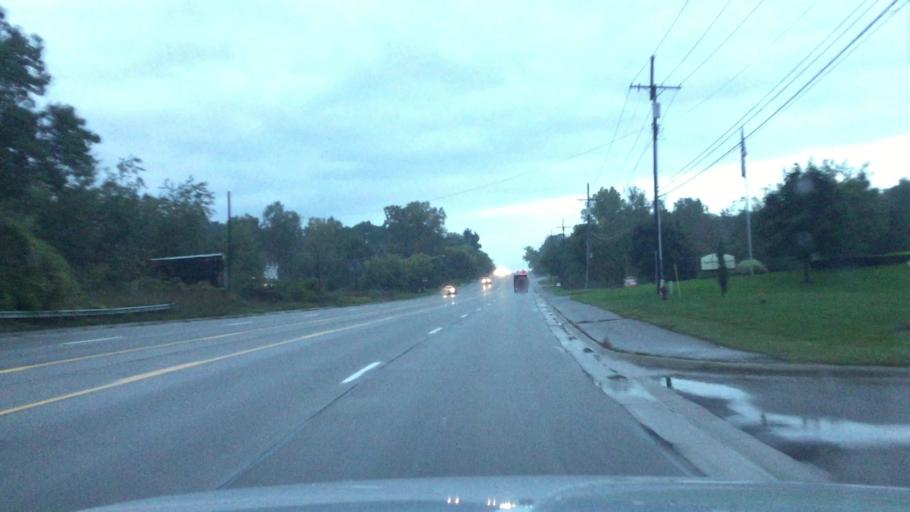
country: US
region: Michigan
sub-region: Oakland County
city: Clarkston
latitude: 42.7302
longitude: -83.4409
